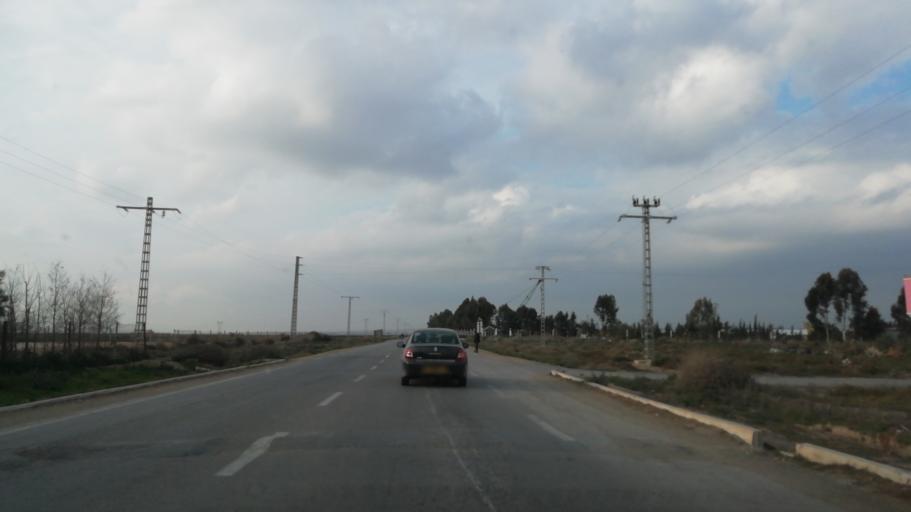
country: DZ
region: Mascara
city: Sig
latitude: 35.6930
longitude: -0.0196
